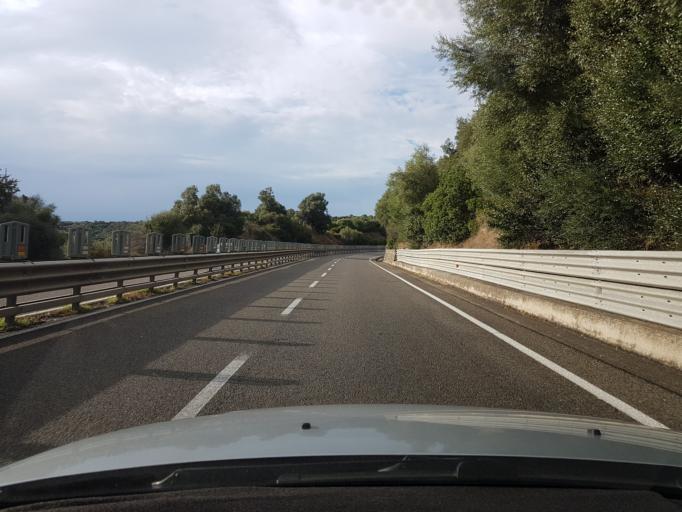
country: IT
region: Sardinia
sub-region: Provincia di Oristano
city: Bauladu
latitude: 40.0484
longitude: 8.7093
